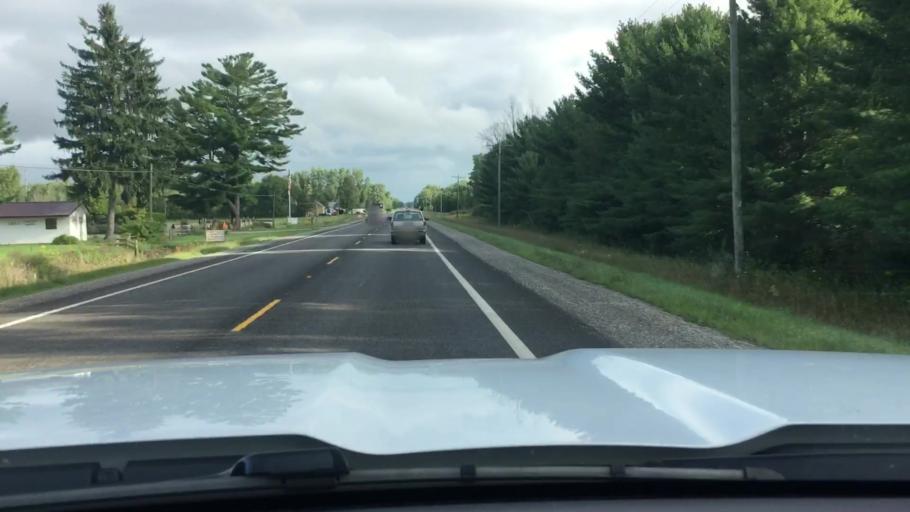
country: US
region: Michigan
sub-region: Tuscola County
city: Caro
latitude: 43.4349
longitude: -83.3850
